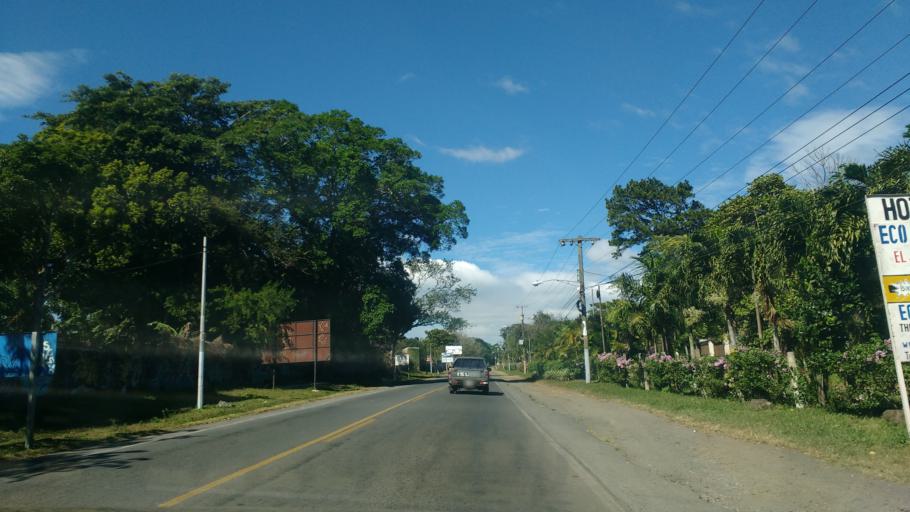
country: NI
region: Carazo
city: Diriamba
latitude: 11.8697
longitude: -86.2390
